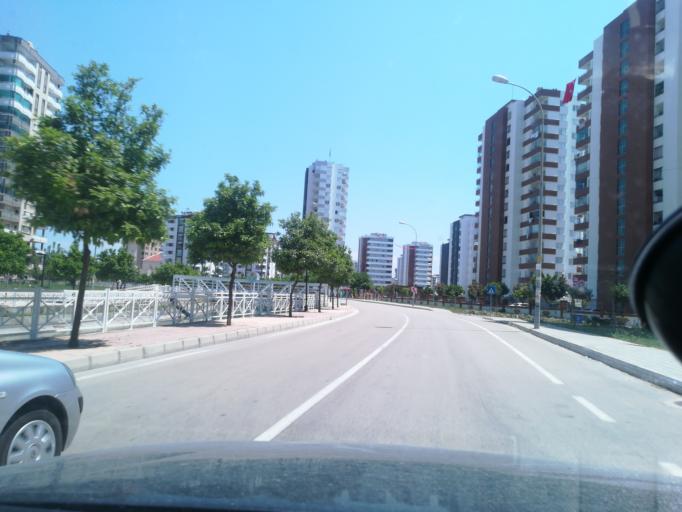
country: TR
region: Adana
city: Seyhan
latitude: 37.0246
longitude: 35.2565
